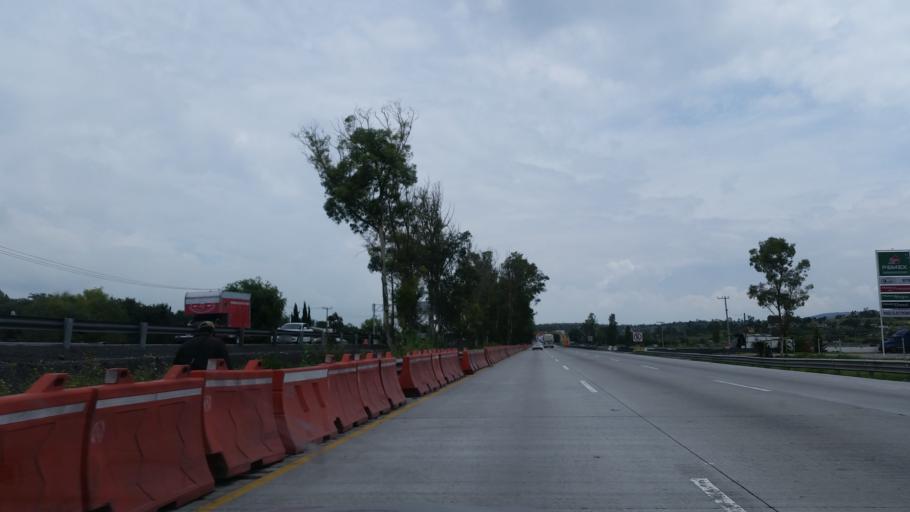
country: MX
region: Mexico
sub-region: Huehuetoca
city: Villa URBI del Rey
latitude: 19.8420
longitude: -99.2783
